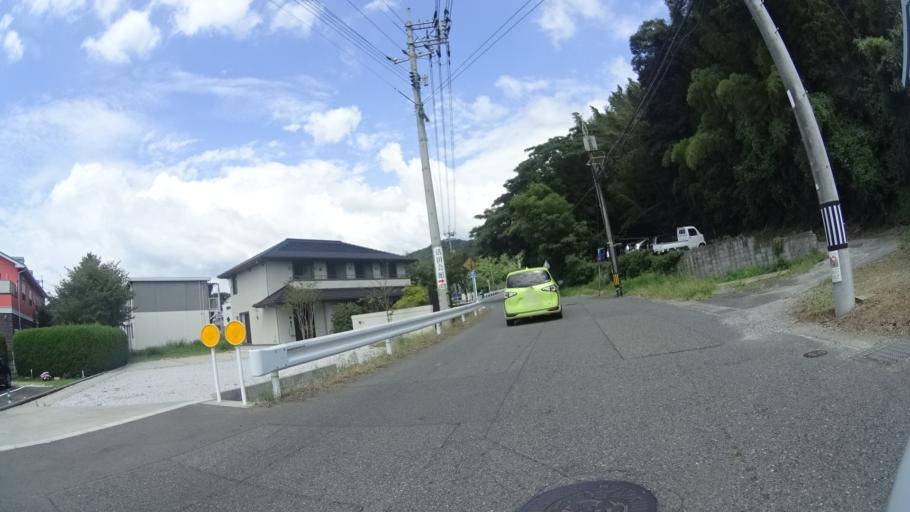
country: JP
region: Yamaguchi
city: Shimonoseki
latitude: 33.9793
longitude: 130.9509
